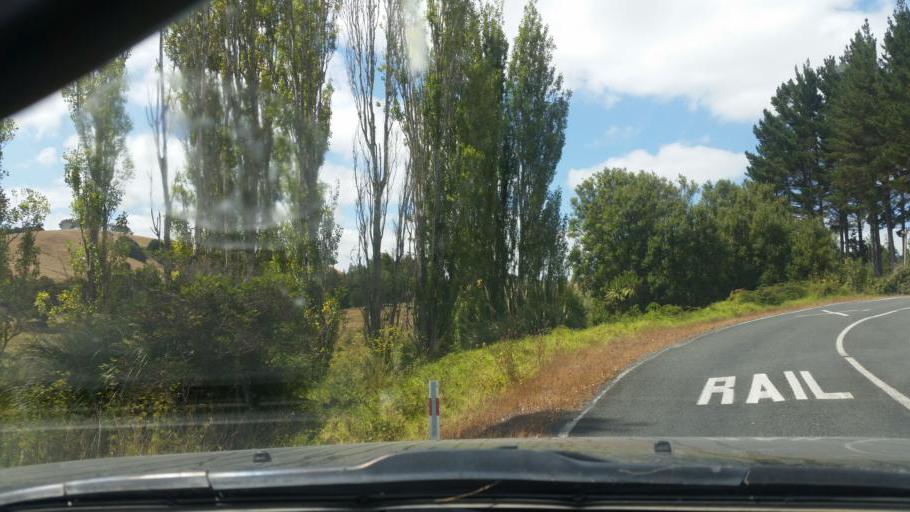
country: NZ
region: Auckland
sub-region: Auckland
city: Wellsford
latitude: -36.1226
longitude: 174.3328
